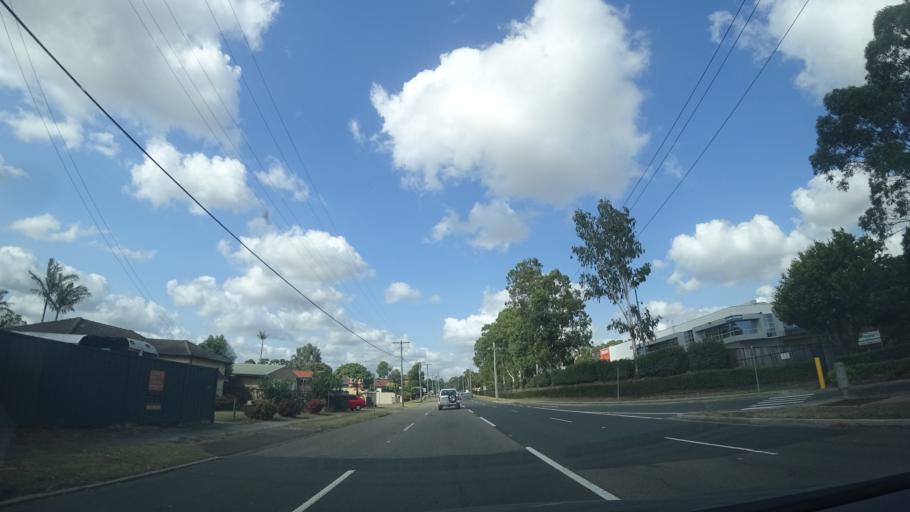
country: AU
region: New South Wales
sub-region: Fairfield
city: Liverpool
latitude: -33.9324
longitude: 150.9291
